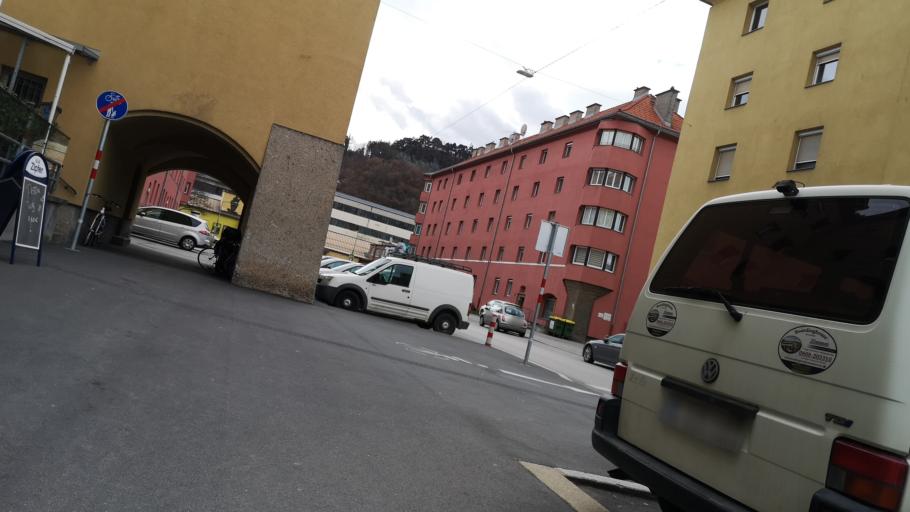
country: AT
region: Tyrol
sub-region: Innsbruck Stadt
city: Innsbruck
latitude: 47.2572
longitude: 11.3902
